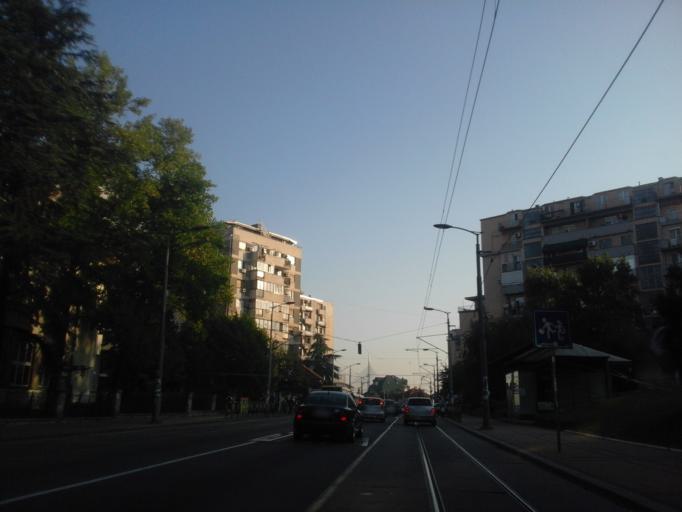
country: RS
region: Central Serbia
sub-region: Belgrade
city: Cukarica
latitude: 44.7803
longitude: 20.4168
